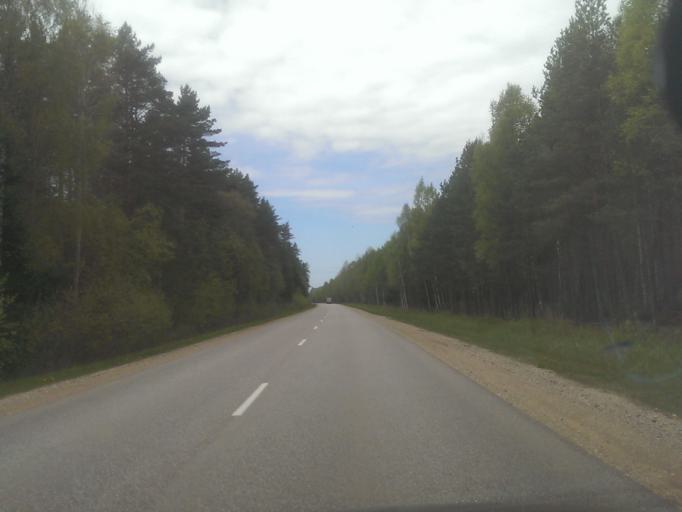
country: LV
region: Ventspils Rajons
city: Piltene
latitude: 57.1586
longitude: 21.6944
